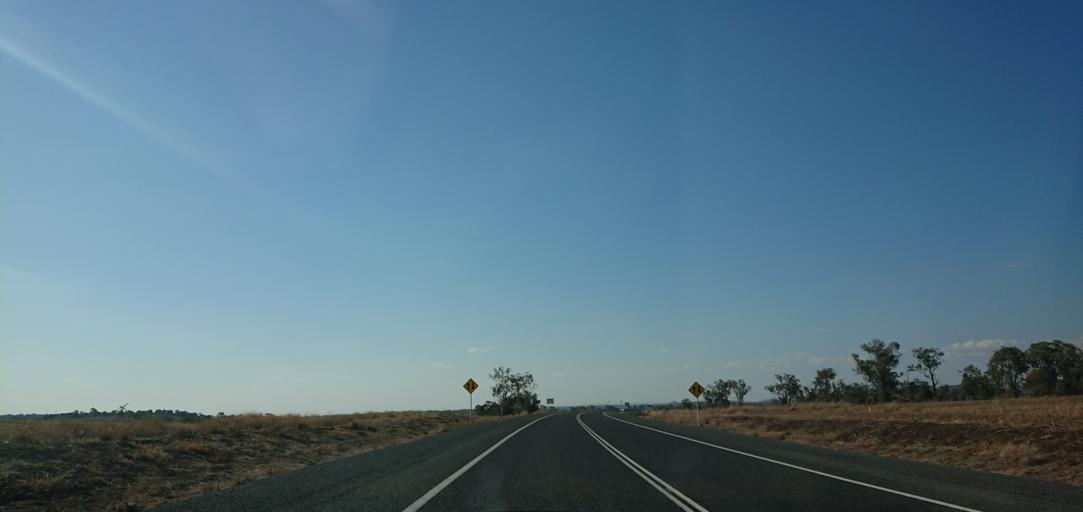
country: AU
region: Queensland
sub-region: Toowoomba
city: Westbrook
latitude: -27.6072
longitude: 151.7861
